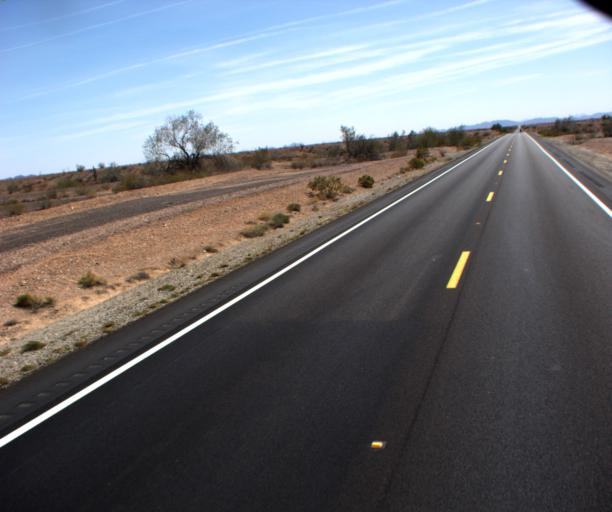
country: US
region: Arizona
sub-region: Yuma County
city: Wellton
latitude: 33.0560
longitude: -114.2921
